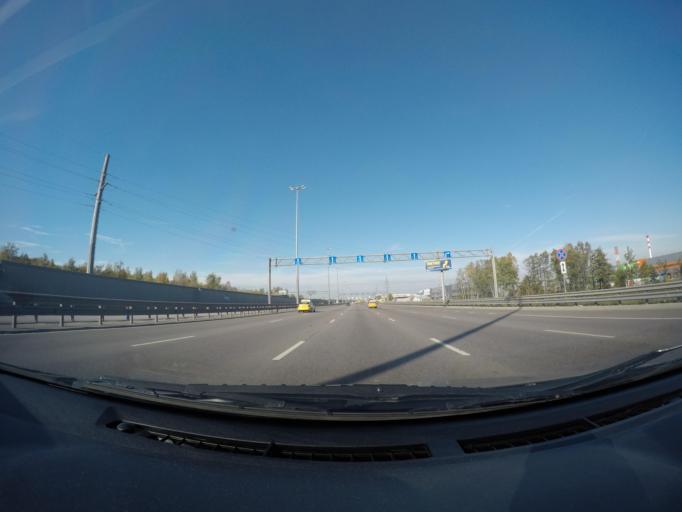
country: RU
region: Moskovskaya
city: Tomilino
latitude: 55.6402
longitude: 37.9219
